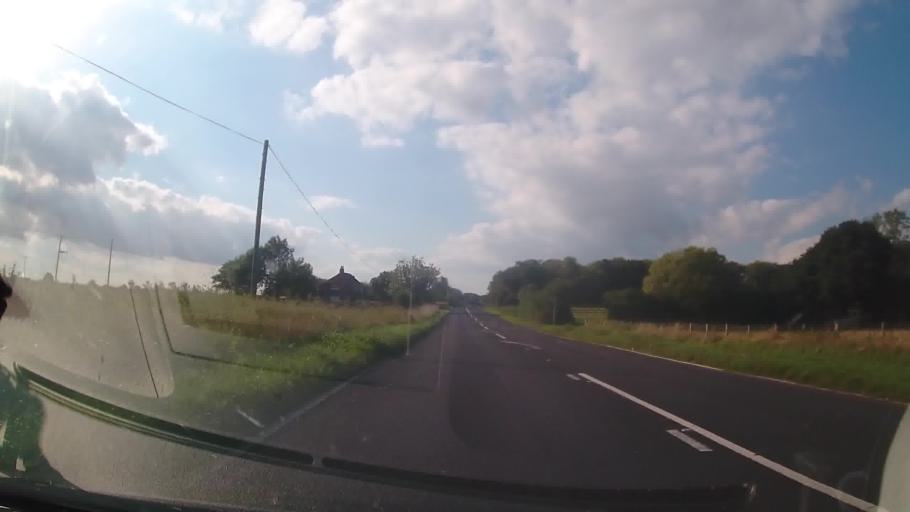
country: GB
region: England
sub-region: Kent
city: Hythe
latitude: 51.0930
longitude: 1.0805
